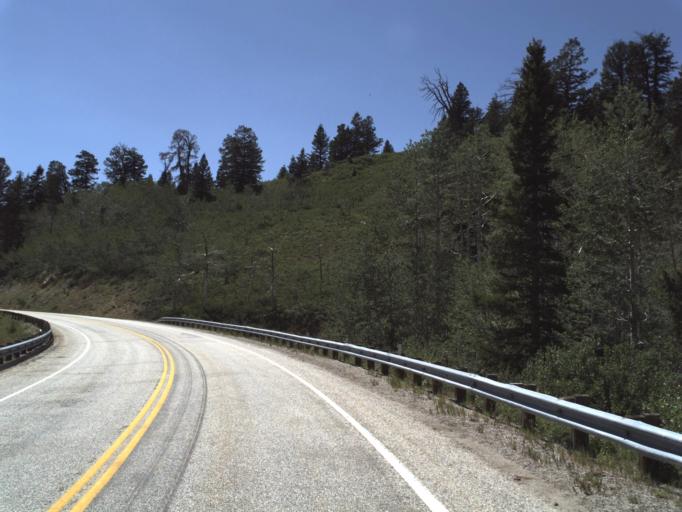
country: US
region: Utah
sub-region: Rich County
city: Randolph
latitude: 41.4761
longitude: -111.4642
